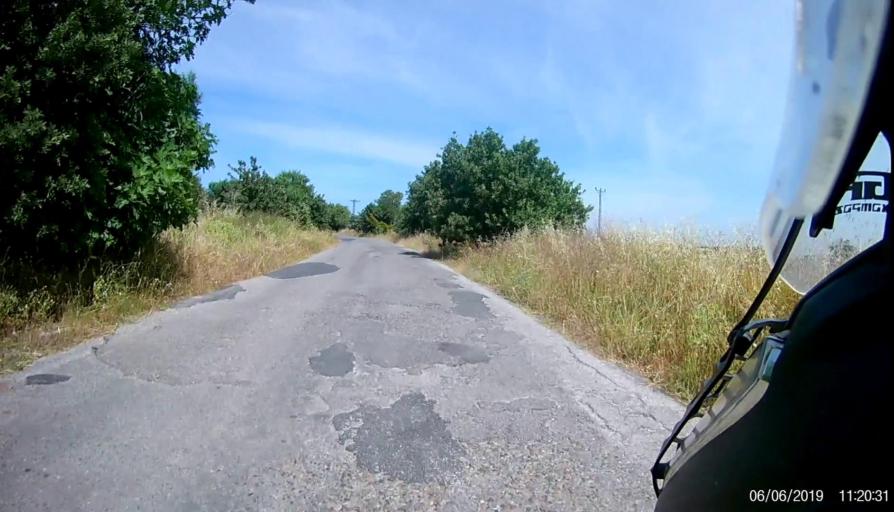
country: TR
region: Canakkale
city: Gulpinar
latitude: 39.6674
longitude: 26.1634
